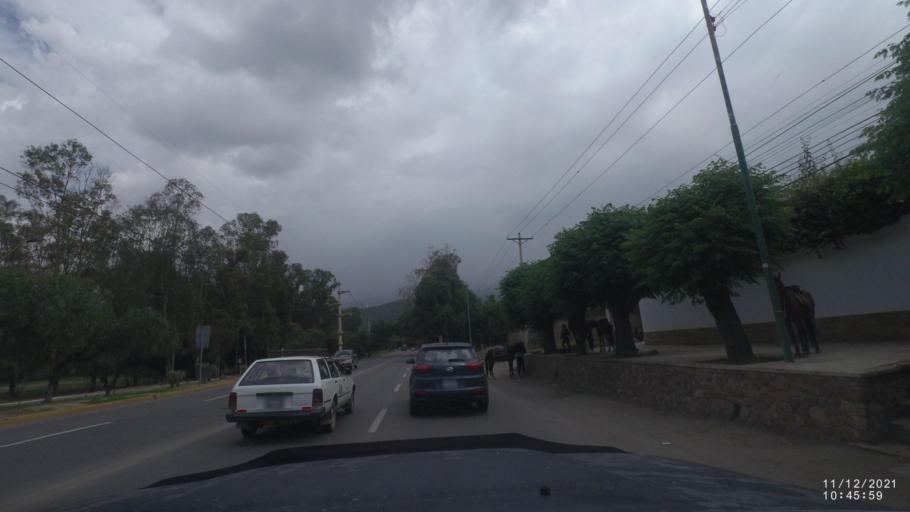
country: BO
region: Cochabamba
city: Cochabamba
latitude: -17.4110
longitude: -66.1265
